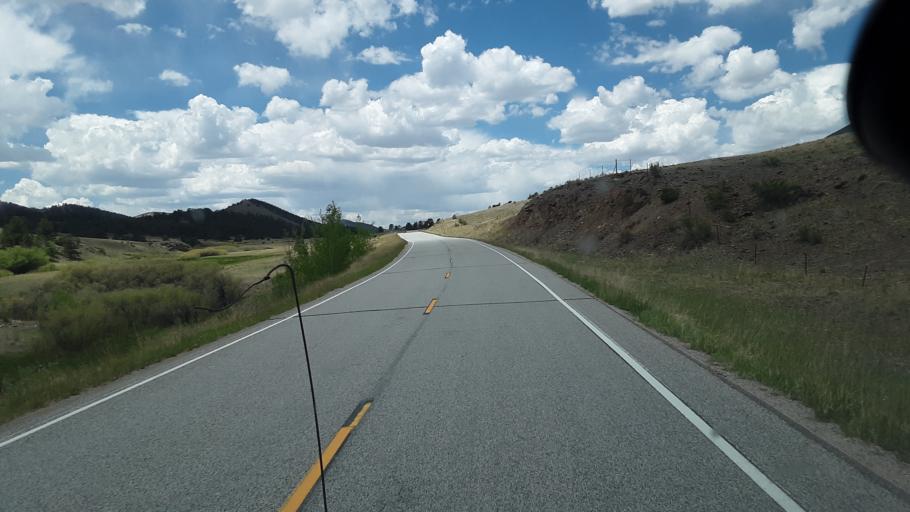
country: US
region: Colorado
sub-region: Teller County
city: Cripple Creek
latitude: 38.7884
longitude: -105.5857
